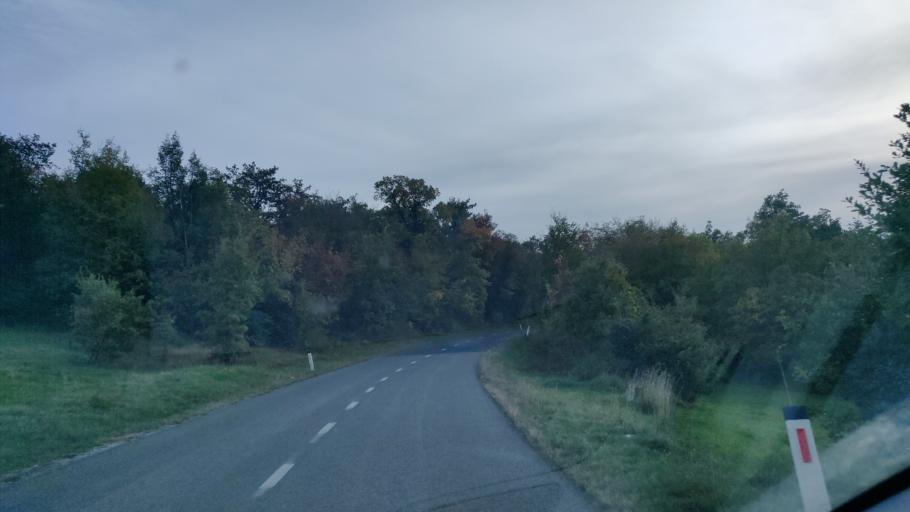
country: SI
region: Sezana
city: Sezana
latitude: 45.7936
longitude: 13.8594
